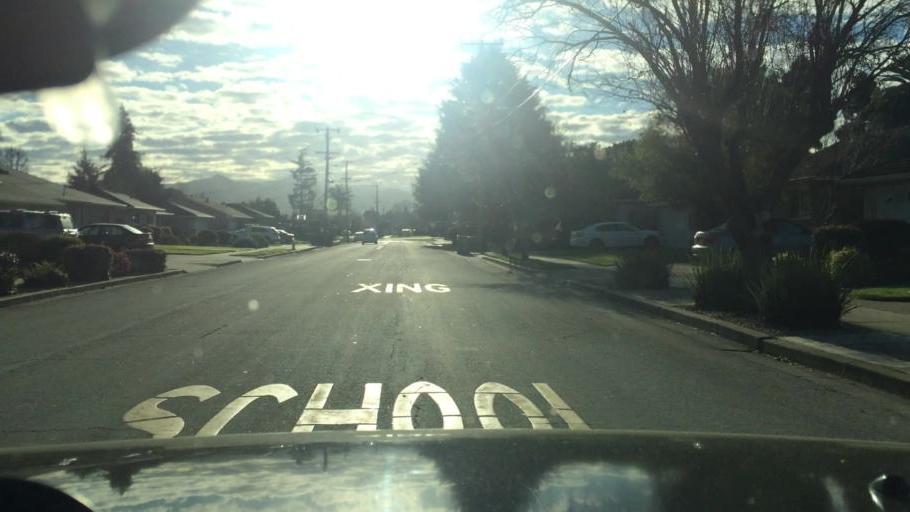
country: US
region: California
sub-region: Alameda County
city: Fremont
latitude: 37.5487
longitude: -121.9984
